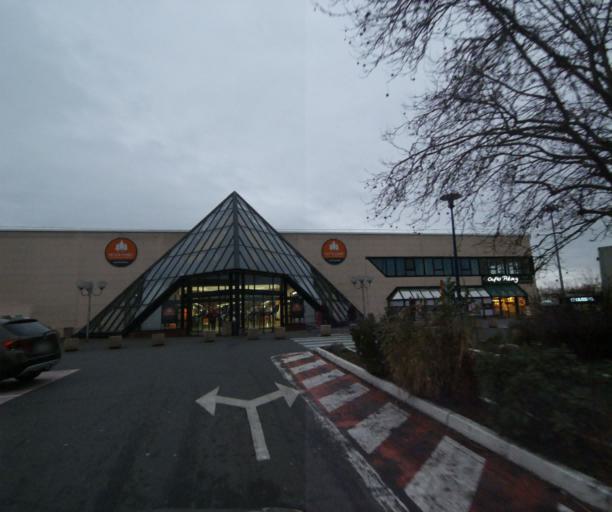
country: FR
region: Nord-Pas-de-Calais
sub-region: Departement du Nord
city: Raismes
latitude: 50.3774
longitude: 3.4775
